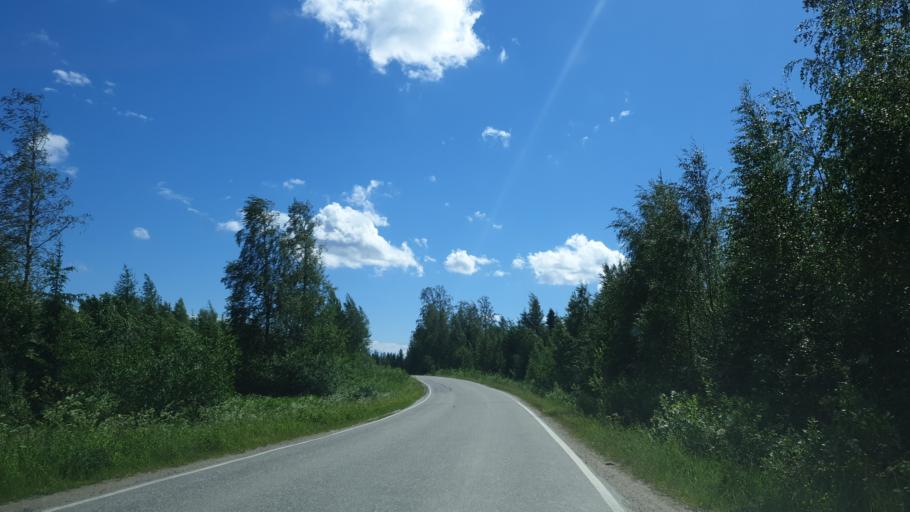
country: FI
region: Northern Savo
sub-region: Koillis-Savo
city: Kaavi
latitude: 62.9985
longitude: 28.5031
